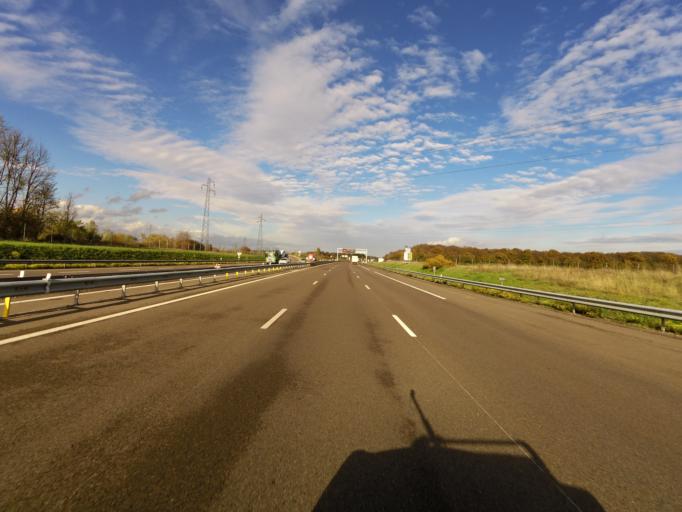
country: FR
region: Bourgogne
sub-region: Departement de la Cote-d'Or
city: Gevrey-Chambertin
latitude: 47.2132
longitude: 5.0009
